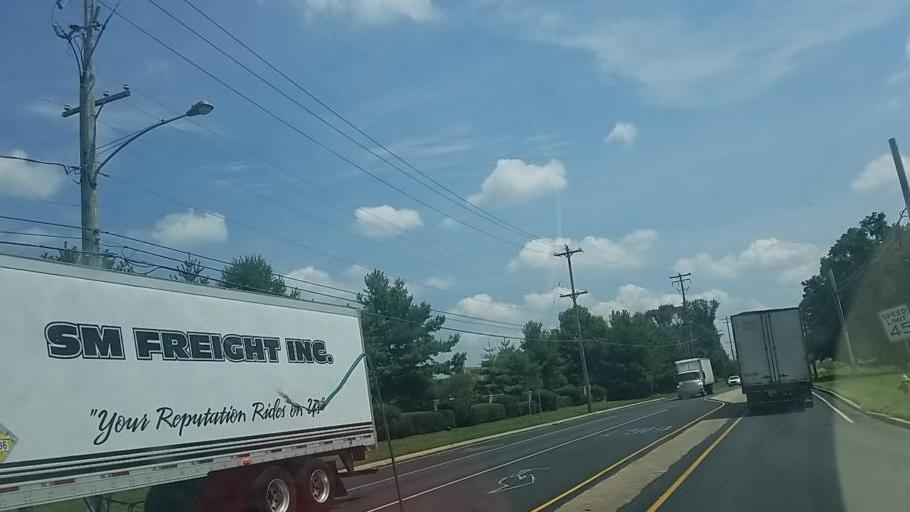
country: US
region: Pennsylvania
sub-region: Chester County
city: Toughkenamon
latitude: 39.8053
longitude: -75.7444
